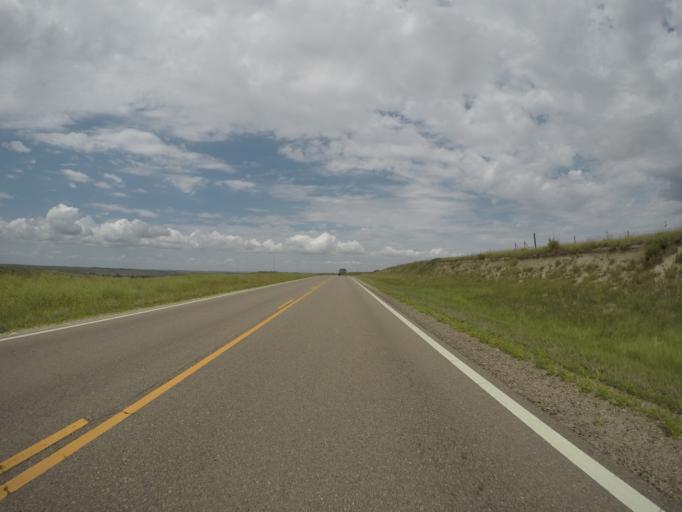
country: US
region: Kansas
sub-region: Rawlins County
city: Atwood
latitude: 39.7729
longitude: -101.0470
